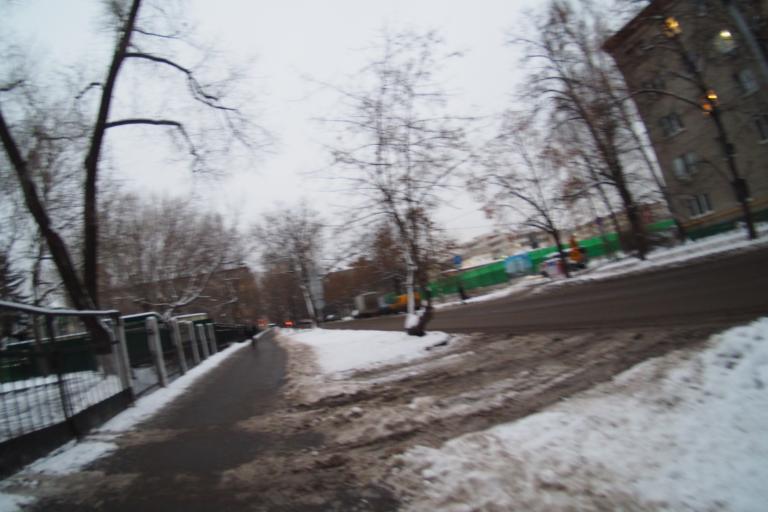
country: RU
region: Moscow
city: Sokol
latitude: 55.7979
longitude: 37.5637
